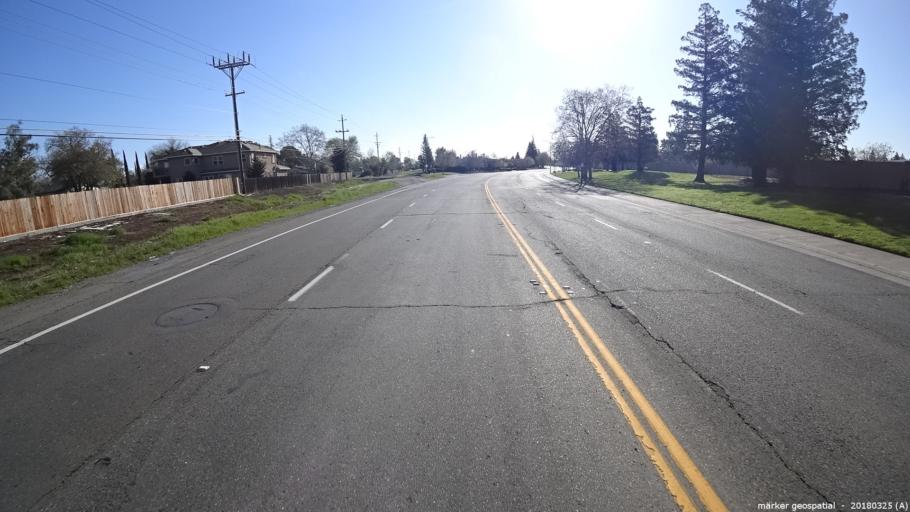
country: US
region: California
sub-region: Sacramento County
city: Rio Linda
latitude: 38.6564
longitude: -121.4834
